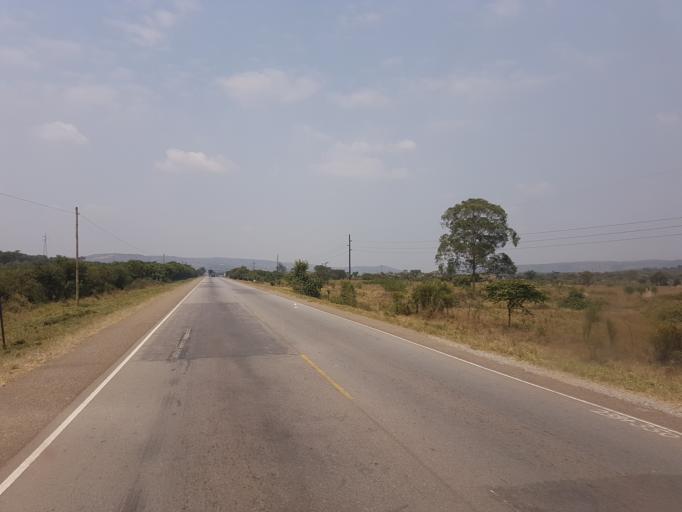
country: UG
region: Western Region
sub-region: Mbarara District
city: Mbarara
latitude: -0.5108
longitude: 30.8176
